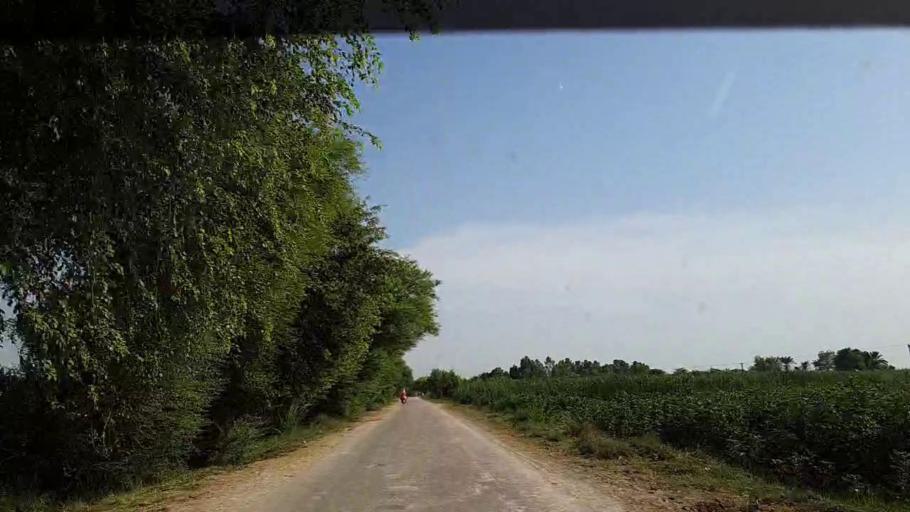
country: PK
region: Sindh
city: Adilpur
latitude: 27.9340
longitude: 69.2544
